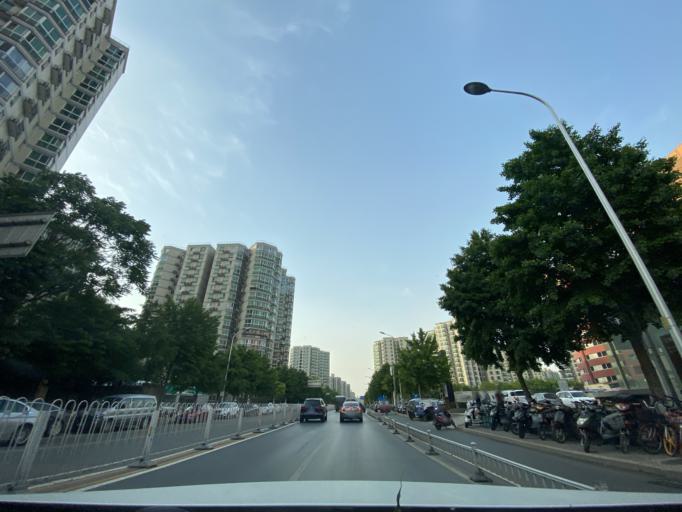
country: CN
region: Beijing
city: Sijiqing
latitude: 39.9569
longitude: 116.2784
